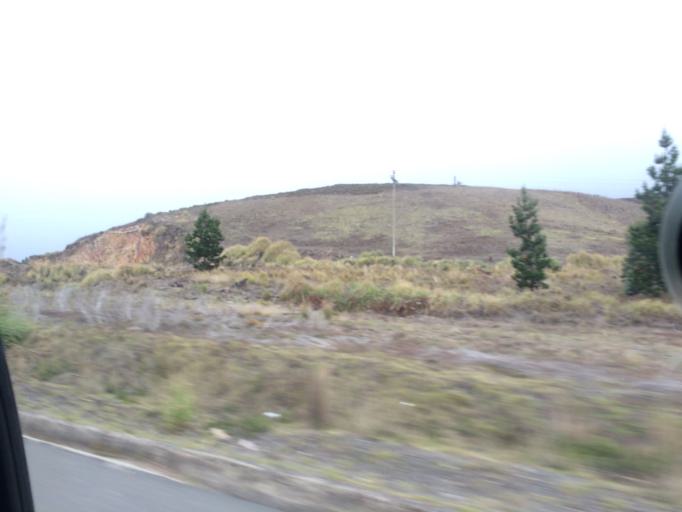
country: EC
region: Chimborazo
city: Alausi
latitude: -2.0756
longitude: -78.7350
